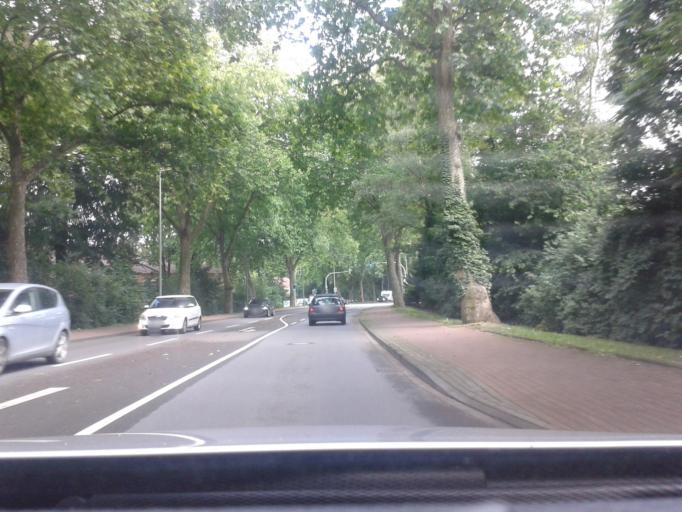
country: DE
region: North Rhine-Westphalia
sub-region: Regierungsbezirk Dusseldorf
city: Hochfeld
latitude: 51.4152
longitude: 6.7156
